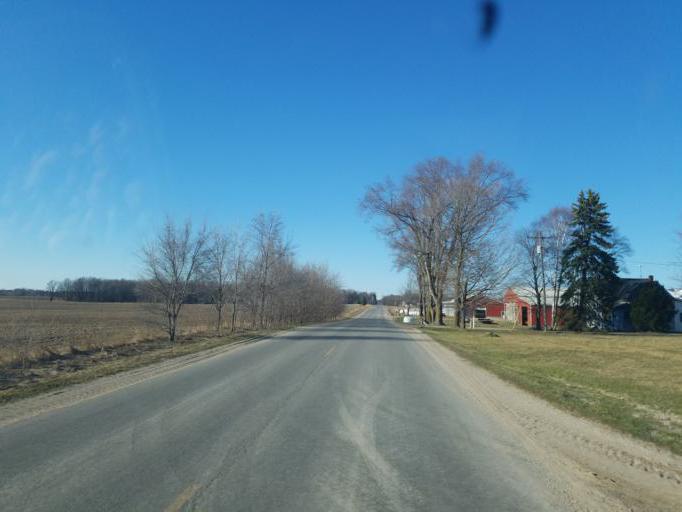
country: US
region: Michigan
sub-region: Montcalm County
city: Lakeview
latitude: 43.5290
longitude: -85.1847
